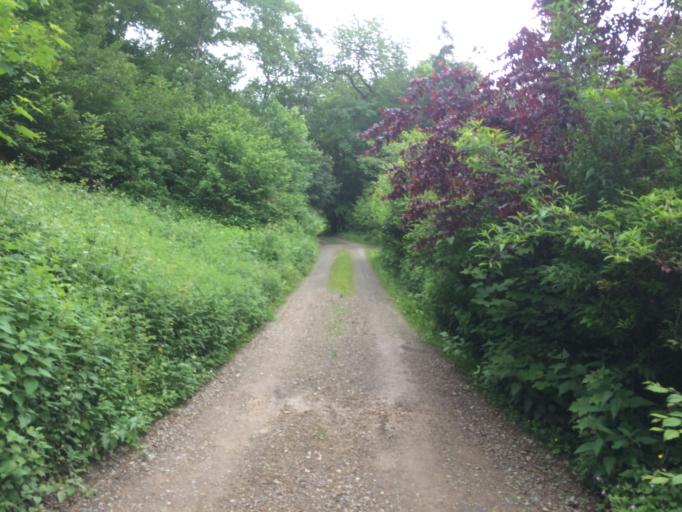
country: BE
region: Wallonia
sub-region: Province de Namur
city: Yvoir
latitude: 50.3216
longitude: 4.9451
